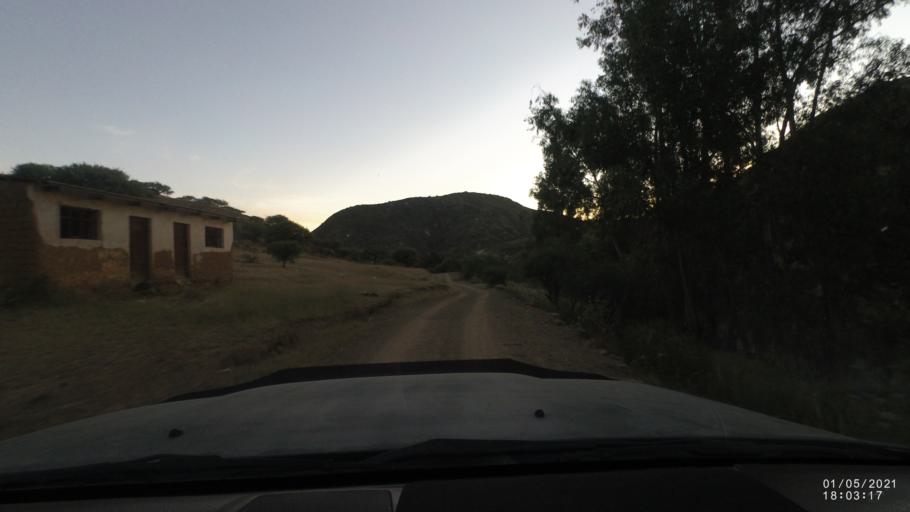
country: BO
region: Cochabamba
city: Capinota
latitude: -17.6887
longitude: -66.1760
